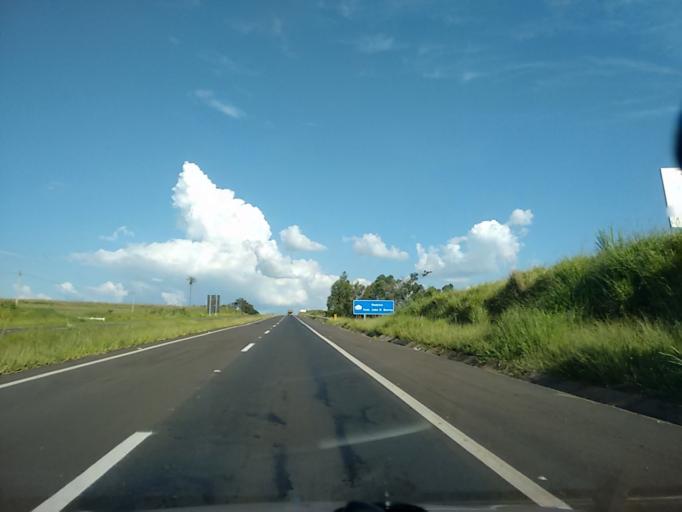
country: BR
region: Sao Paulo
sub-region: Garca
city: Garca
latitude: -22.2631
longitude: -49.5225
